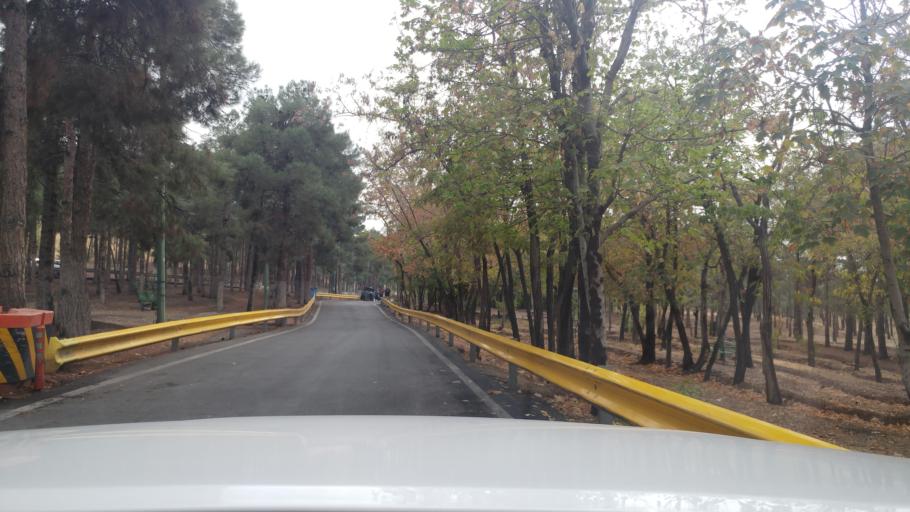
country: IR
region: Tehran
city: Shahr-e Qods
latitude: 35.7232
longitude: 51.2221
